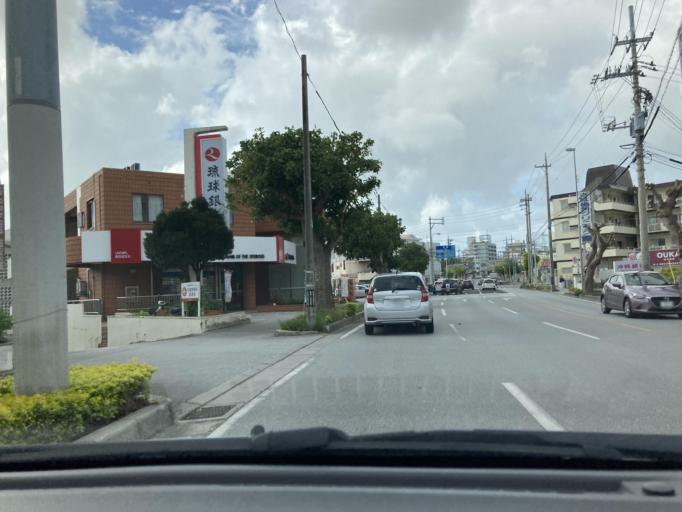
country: JP
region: Okinawa
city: Tomigusuku
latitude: 26.1759
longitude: 127.6826
